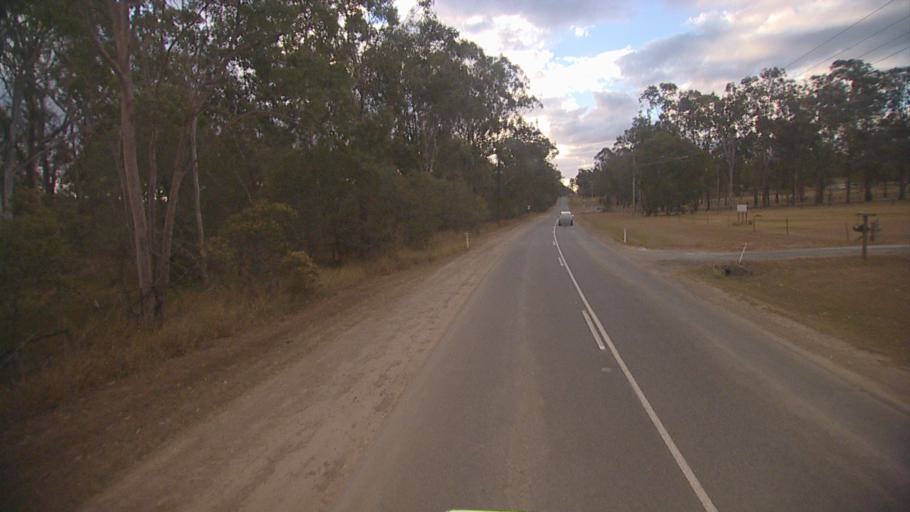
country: AU
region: Queensland
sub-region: Logan
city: Cedar Vale
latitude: -27.8614
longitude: 153.0563
